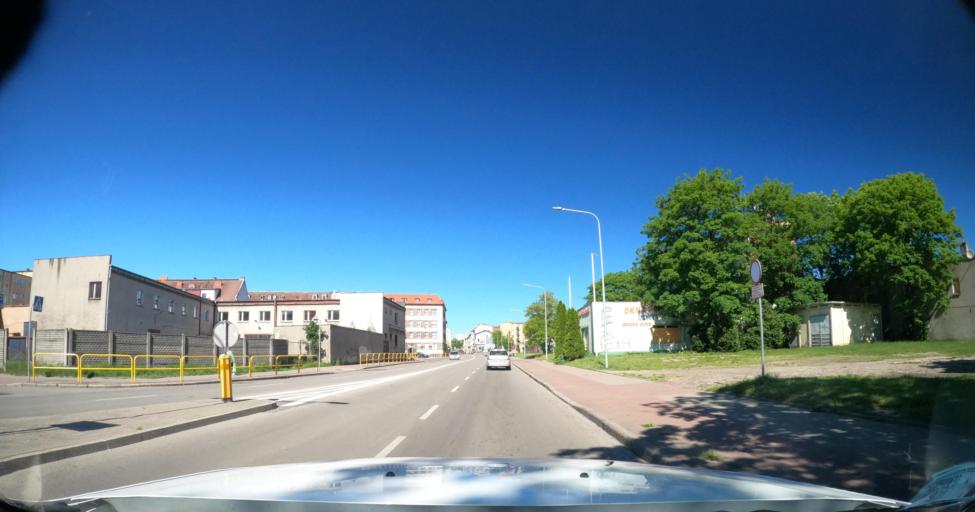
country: PL
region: Pomeranian Voivodeship
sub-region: Slupsk
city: Slupsk
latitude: 54.4707
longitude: 17.0271
